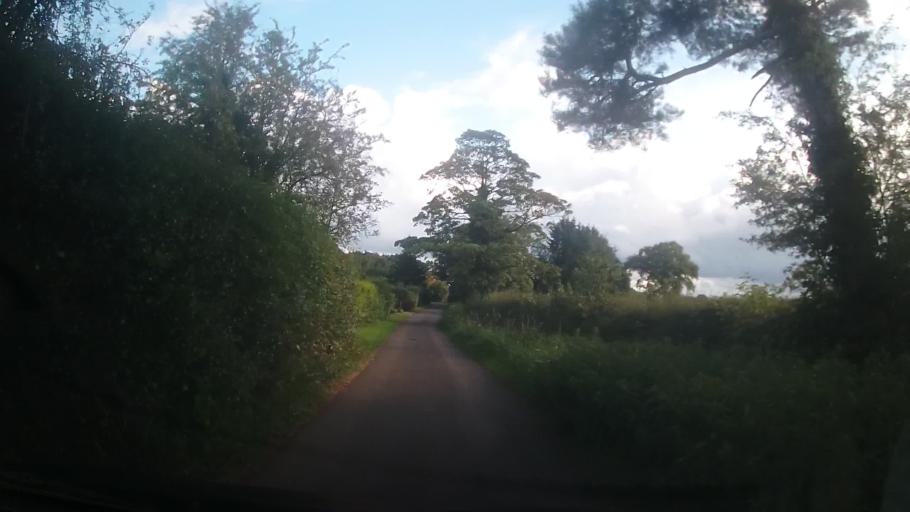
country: GB
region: England
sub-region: Shropshire
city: Wem
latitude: 52.8839
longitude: -2.7356
